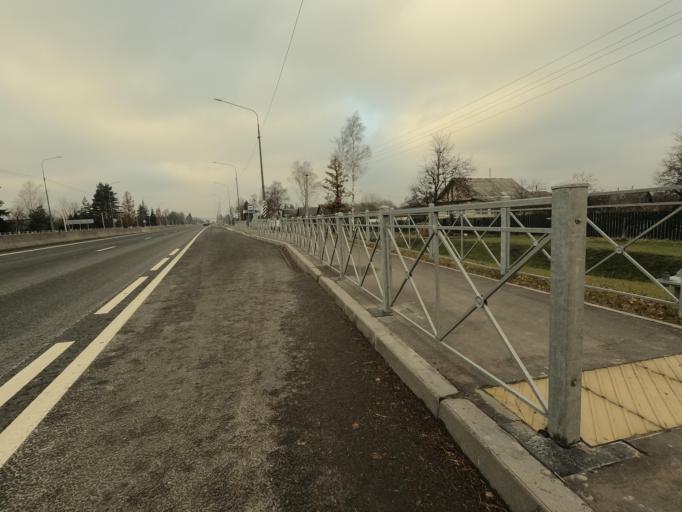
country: RU
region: Leningrad
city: Mga
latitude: 59.7175
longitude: 31.1089
